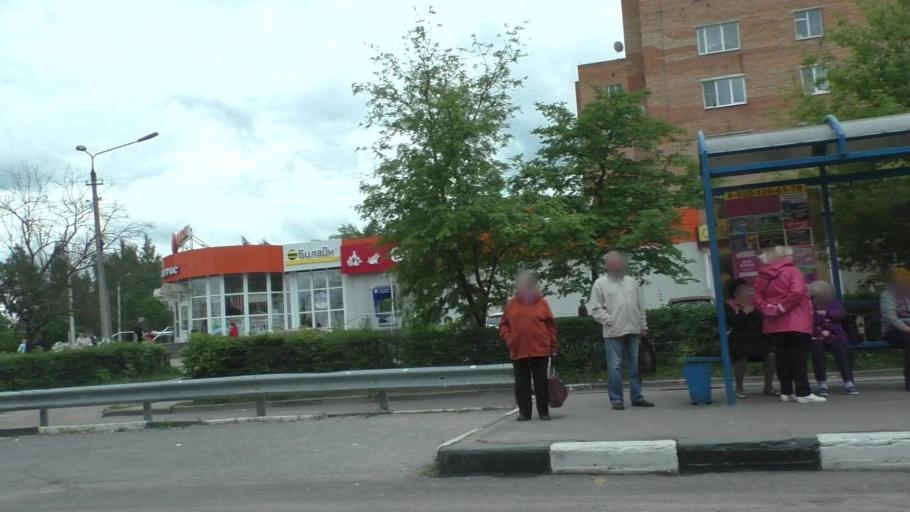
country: RU
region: Moskovskaya
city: Yegor'yevsk
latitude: 55.3690
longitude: 39.0661
